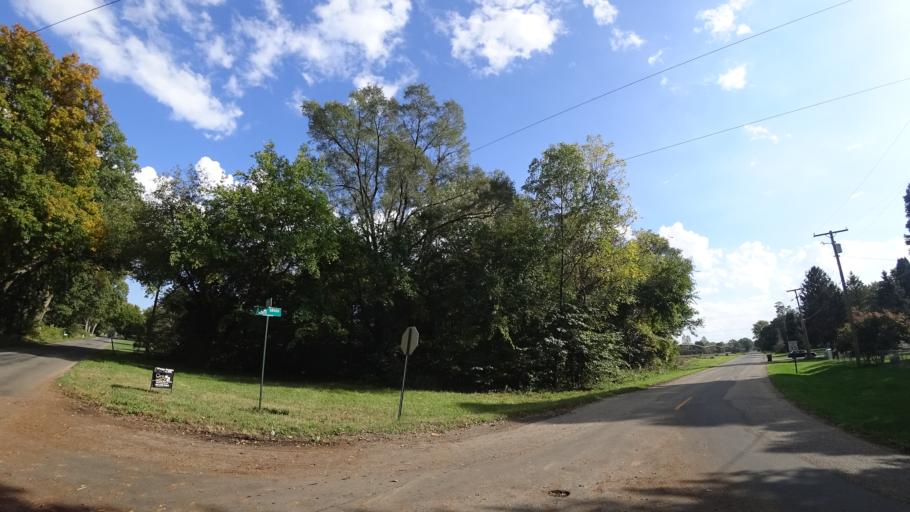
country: US
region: Michigan
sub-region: Saint Joseph County
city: Three Rivers
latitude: 41.9475
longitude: -85.6043
